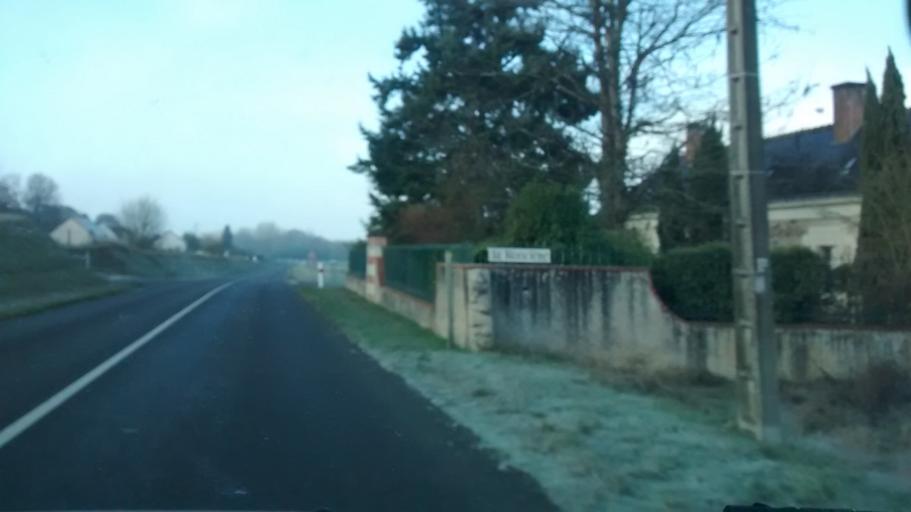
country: FR
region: Centre
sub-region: Departement d'Indre-et-Loire
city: Ballan-Mire
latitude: 47.3550
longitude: 0.5849
